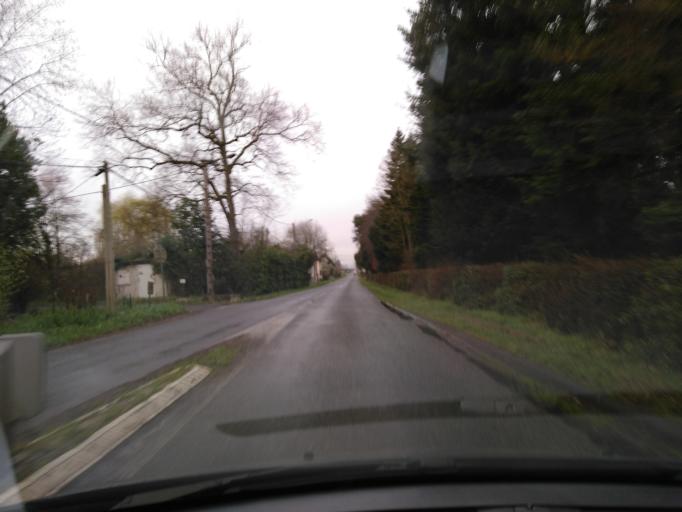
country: FR
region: Midi-Pyrenees
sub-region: Departement de la Haute-Garonne
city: Montesquieu-Volvestre
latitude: 43.1640
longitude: 1.2737
